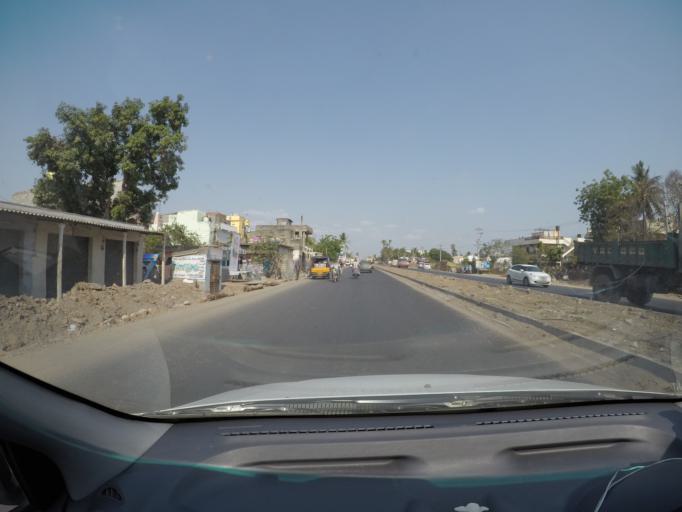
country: IN
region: Andhra Pradesh
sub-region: Krishna
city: Yanamalakuduru
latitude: 16.4753
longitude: 80.7095
